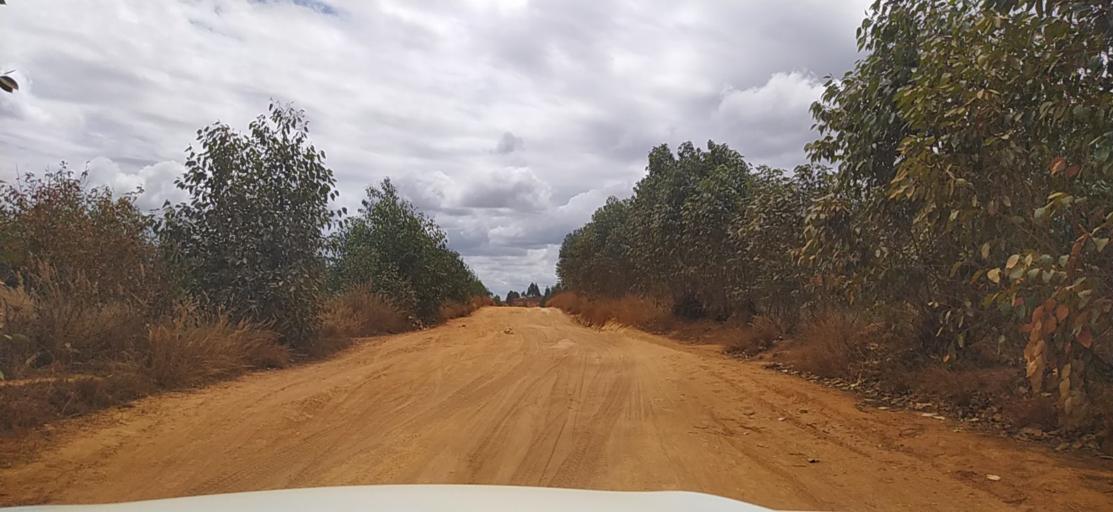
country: MG
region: Alaotra Mangoro
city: Ambatondrazaka
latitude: -18.0634
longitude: 48.2571
